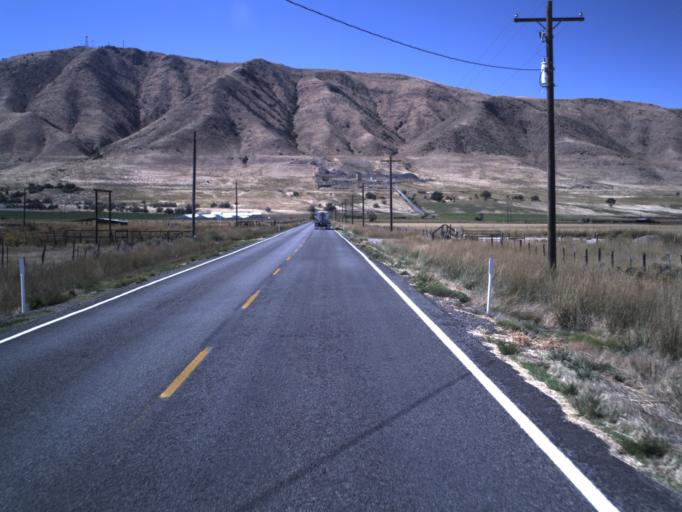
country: US
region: Utah
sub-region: Utah County
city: West Mountain
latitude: 40.0979
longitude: -111.7786
